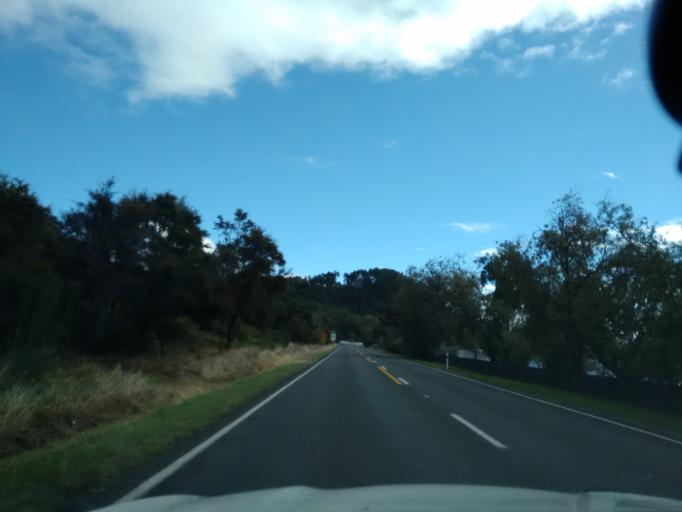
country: NZ
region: Waikato
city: Turangi
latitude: -38.8863
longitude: 175.9629
